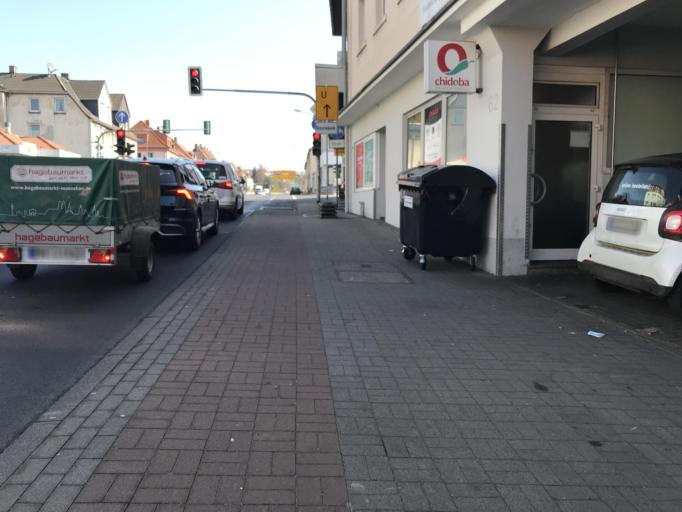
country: DE
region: Hesse
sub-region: Regierungsbezirk Kassel
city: Fulda
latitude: 50.5517
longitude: 9.6925
